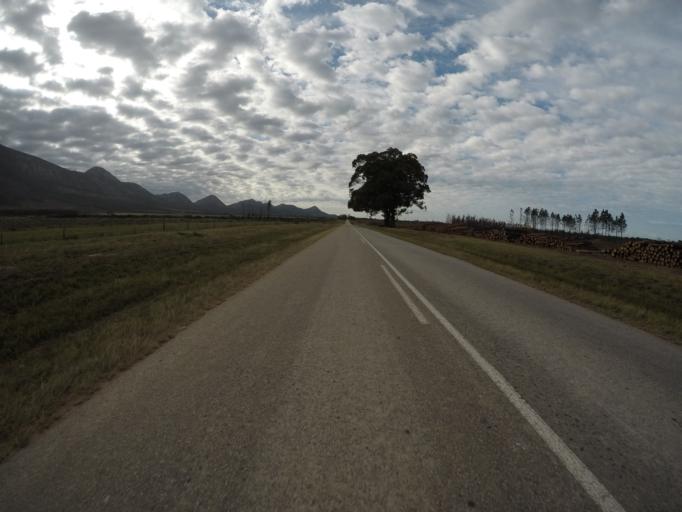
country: ZA
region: Eastern Cape
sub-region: Cacadu District Municipality
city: Kareedouw
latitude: -34.0427
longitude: 24.4178
